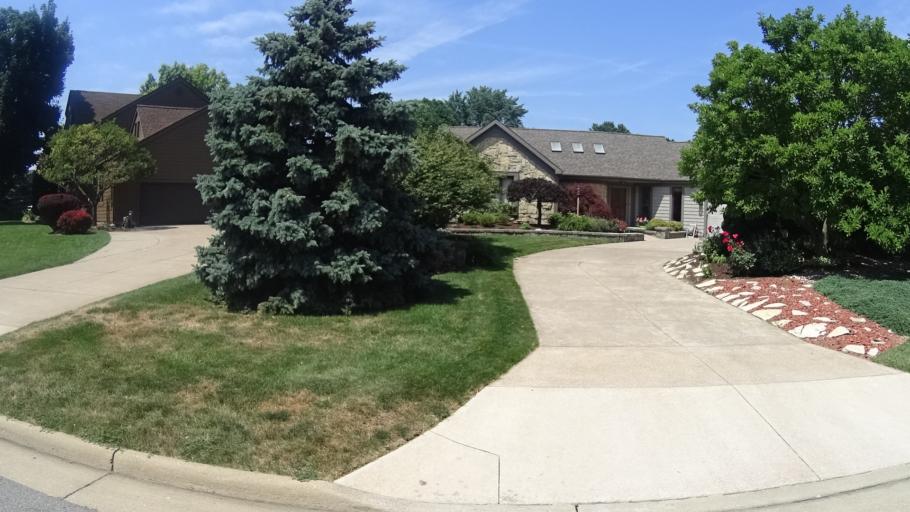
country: US
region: Ohio
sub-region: Erie County
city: Sandusky
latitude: 41.4190
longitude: -82.6447
